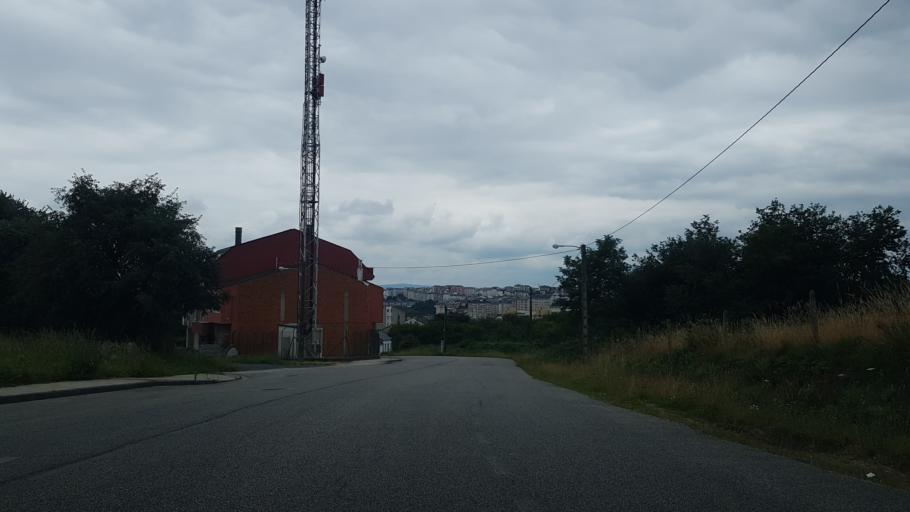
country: ES
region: Galicia
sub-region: Provincia de Lugo
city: Lugo
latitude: 43.0210
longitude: -7.5499
